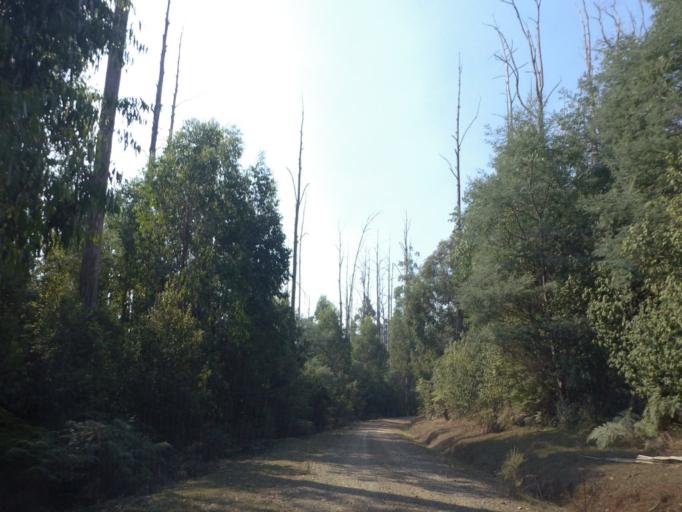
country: AU
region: Victoria
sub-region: Yarra Ranges
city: Millgrove
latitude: -37.5369
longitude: 145.7403
